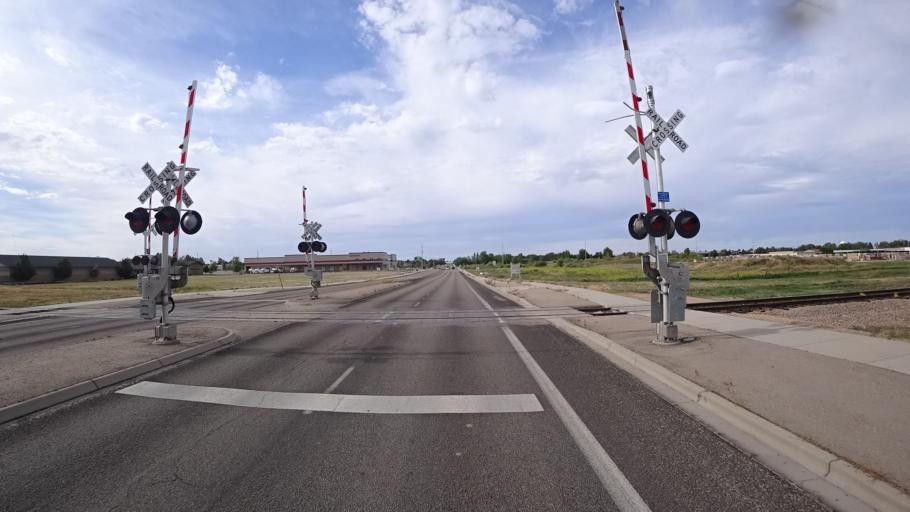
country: US
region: Idaho
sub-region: Ada County
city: Meridian
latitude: 43.6086
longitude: -116.3745
